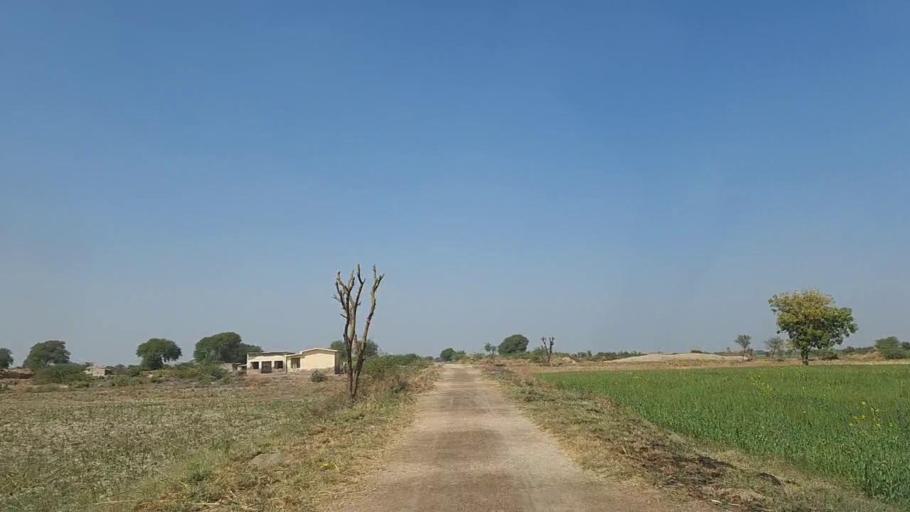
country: PK
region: Sindh
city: Digri
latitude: 25.2065
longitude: 69.1439
